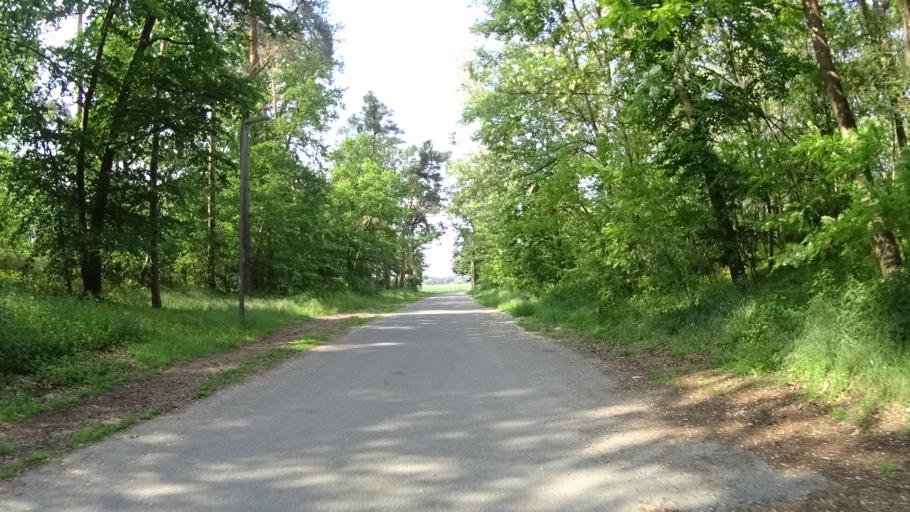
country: DE
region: Baden-Wuerttemberg
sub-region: Karlsruhe Region
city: Reilingen
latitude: 49.2993
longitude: 8.5901
